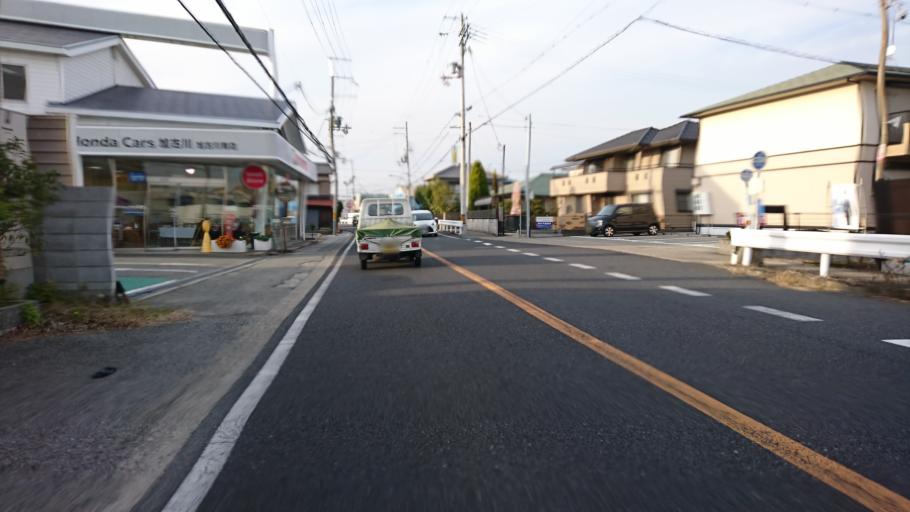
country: JP
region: Hyogo
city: Kakogawacho-honmachi
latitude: 34.7457
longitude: 134.8189
